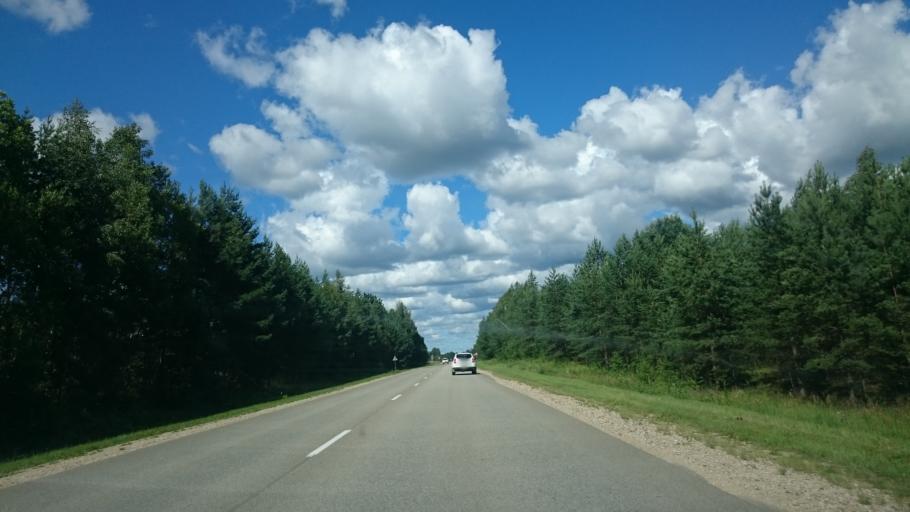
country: LV
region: Kuldigas Rajons
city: Kuldiga
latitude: 56.9532
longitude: 21.9407
